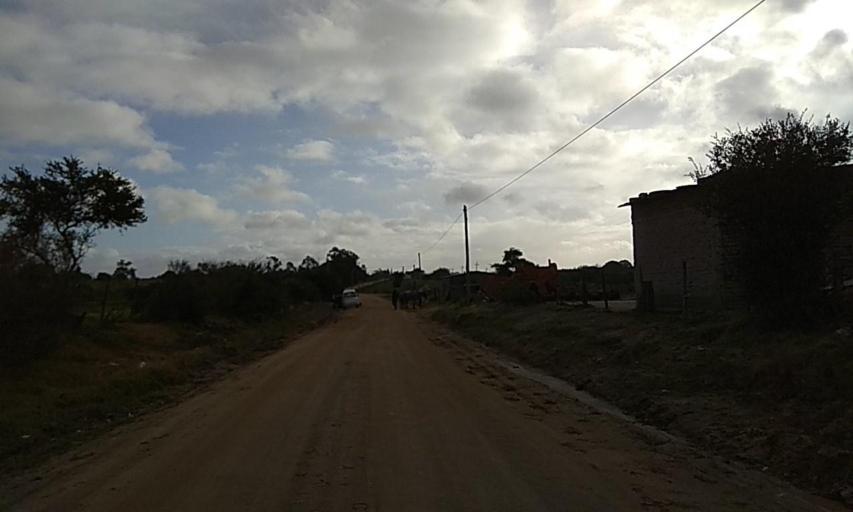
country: UY
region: Florida
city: Florida
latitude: -34.0649
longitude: -56.1935
